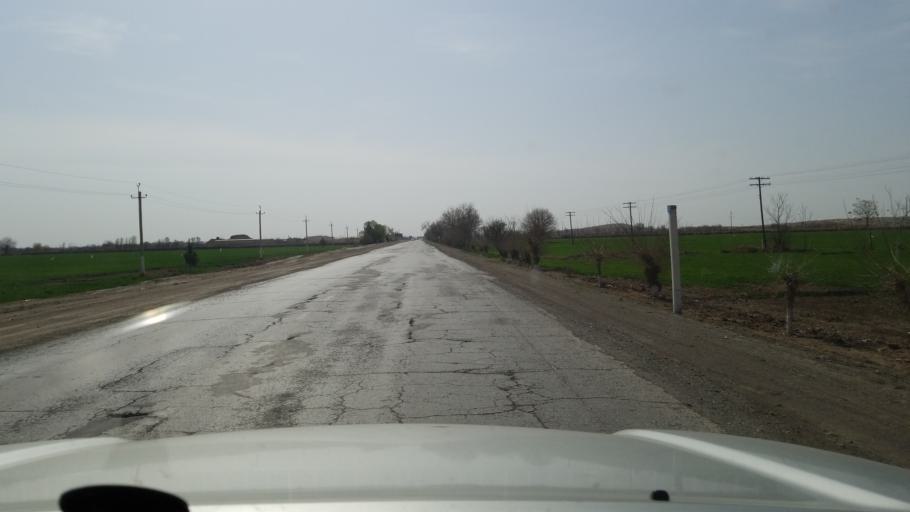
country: TM
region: Lebap
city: Sayat
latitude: 38.8429
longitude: 63.8143
